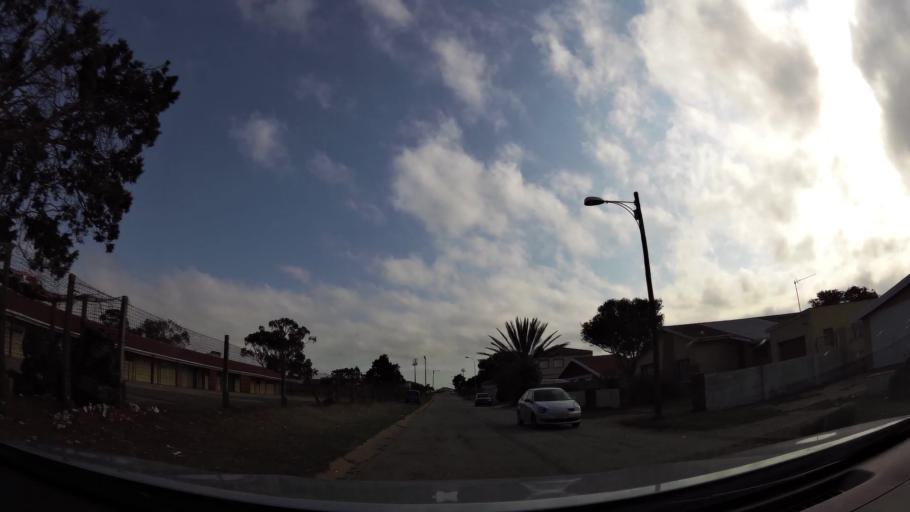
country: ZA
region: Eastern Cape
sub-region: Nelson Mandela Bay Metropolitan Municipality
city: Port Elizabeth
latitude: -33.9189
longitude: 25.5626
